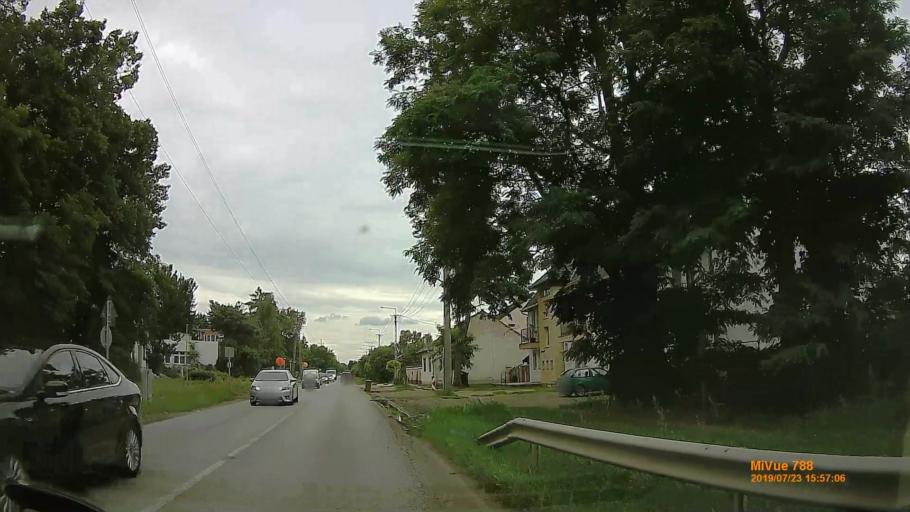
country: HU
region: Szabolcs-Szatmar-Bereg
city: Nyiregyhaza
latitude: 47.9763
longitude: 21.7059
